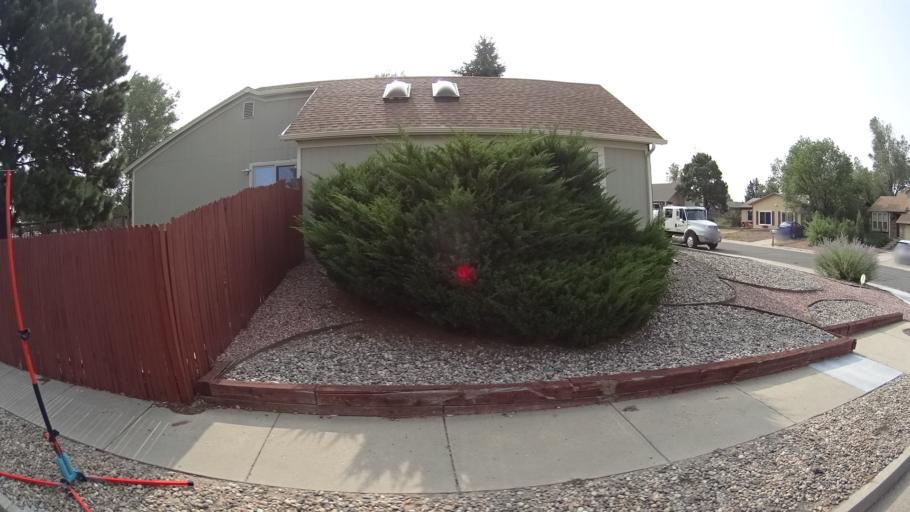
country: US
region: Colorado
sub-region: El Paso County
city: Stratmoor
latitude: 38.8071
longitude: -104.7427
